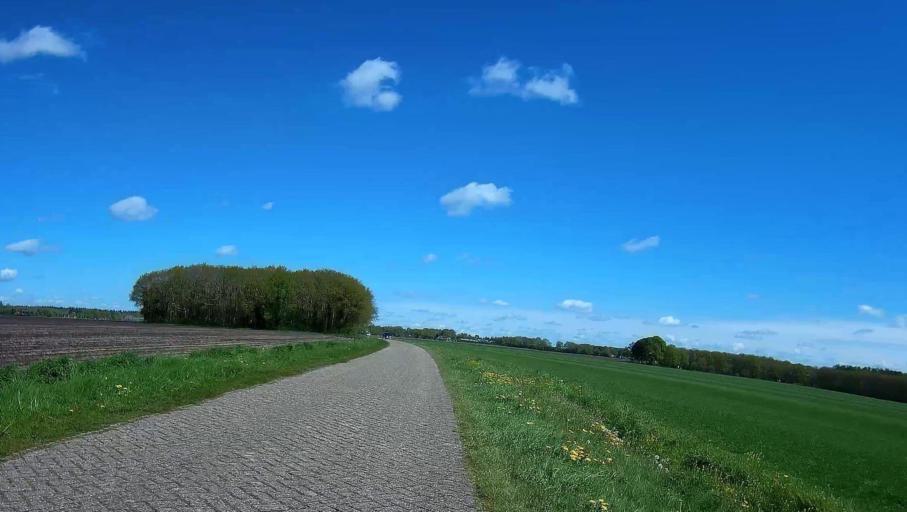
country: NL
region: Drenthe
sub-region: Gemeente Borger-Odoorn
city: Borger
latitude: 52.9405
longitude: 6.7972
